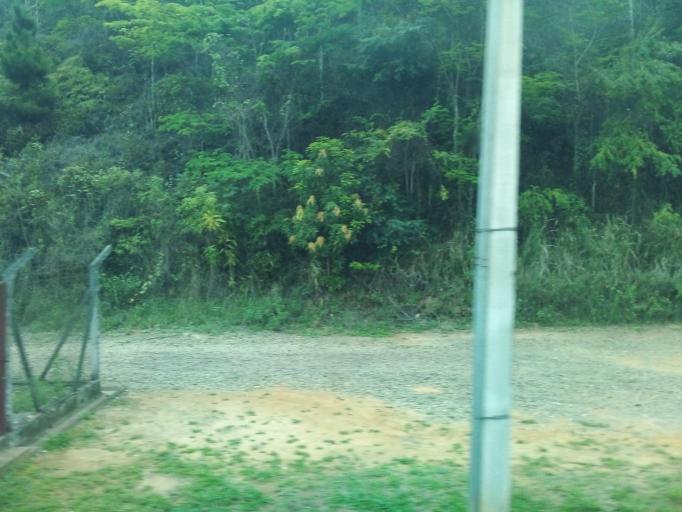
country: BR
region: Minas Gerais
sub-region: Nova Era
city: Nova Era
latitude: -19.7303
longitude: -42.9838
